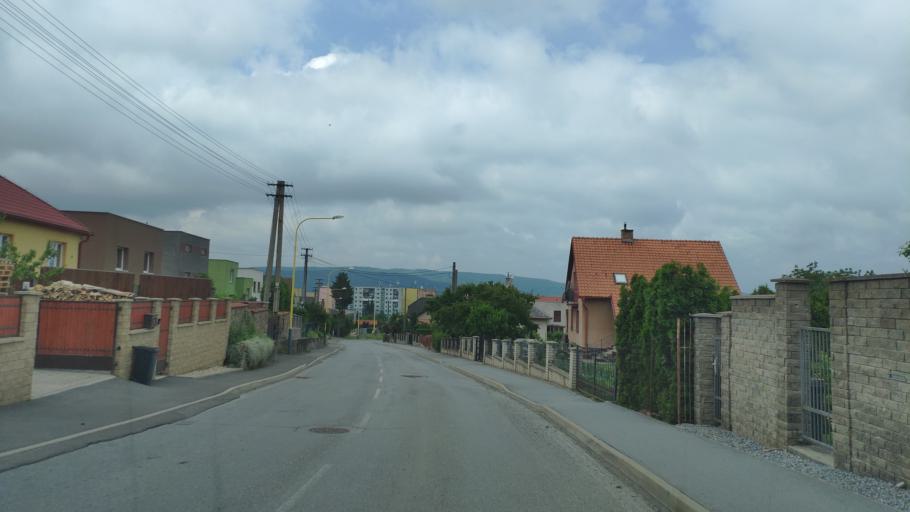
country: SK
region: Presovsky
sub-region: Okres Presov
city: Presov
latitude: 48.9948
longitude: 21.2813
